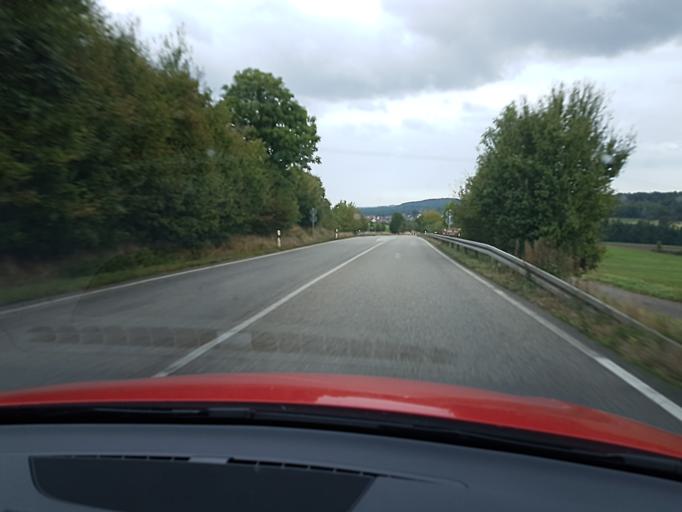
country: DE
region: Baden-Wuerttemberg
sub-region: Karlsruhe Region
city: Muhlacker
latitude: 48.9812
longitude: 8.8462
